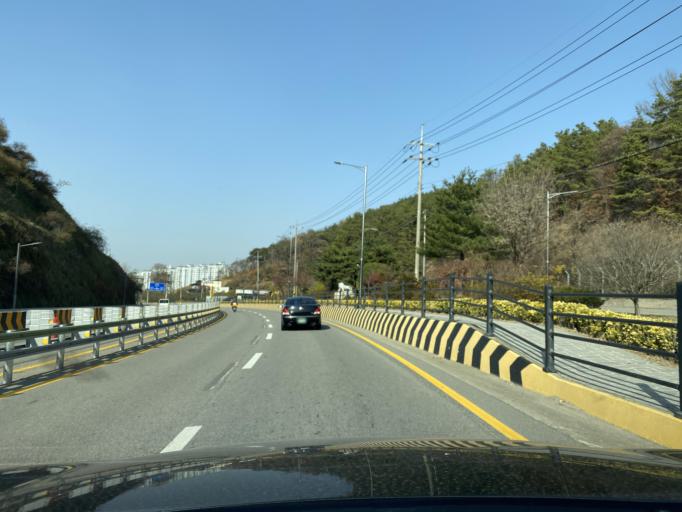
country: KR
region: Chungcheongnam-do
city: Yesan
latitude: 36.6901
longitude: 126.8417
